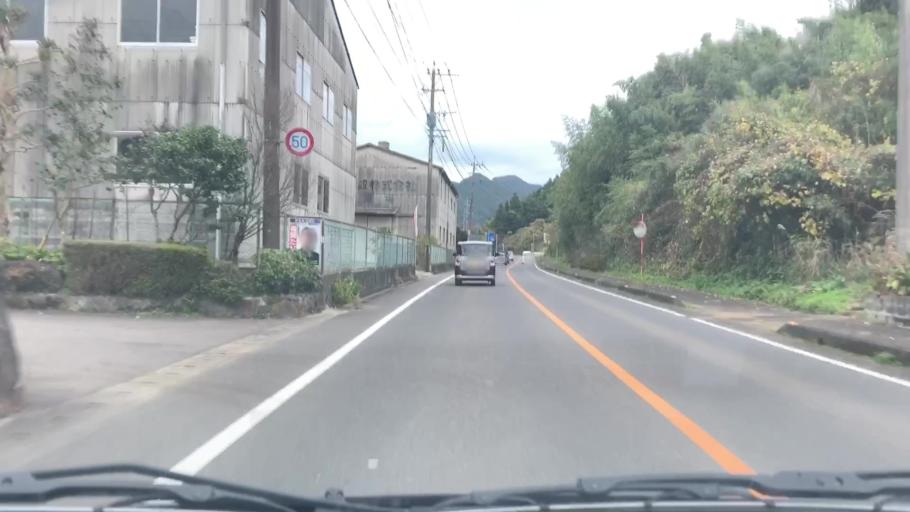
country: JP
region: Saga Prefecture
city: Ureshinomachi-shimojuku
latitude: 33.0894
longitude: 130.0099
